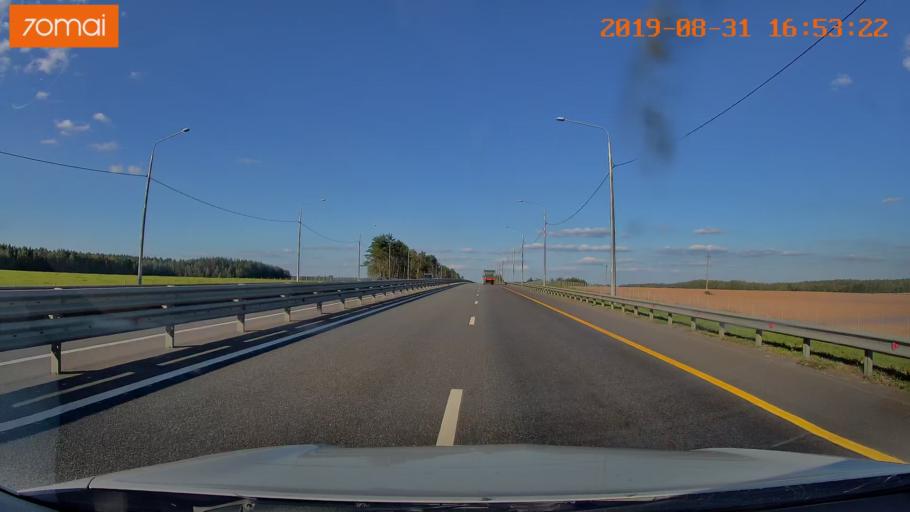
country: RU
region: Kaluga
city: Detchino
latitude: 54.7547
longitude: 36.2106
